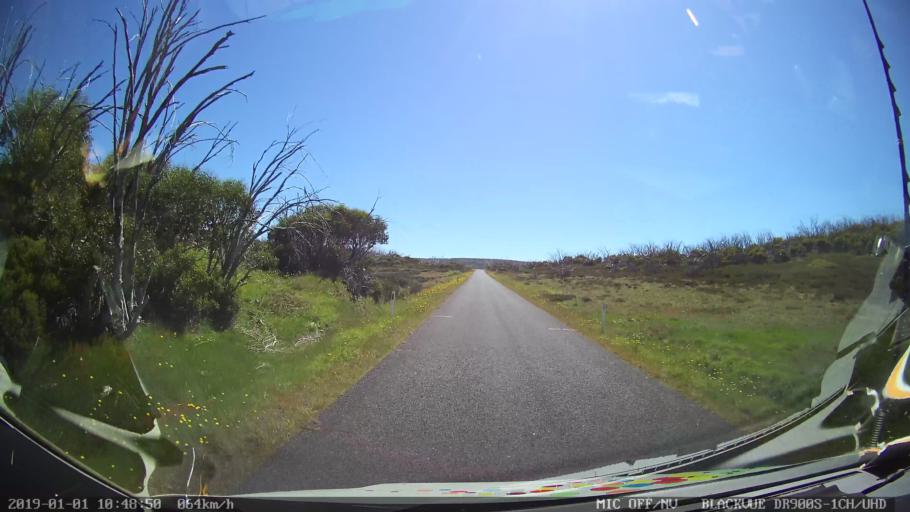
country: AU
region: New South Wales
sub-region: Snowy River
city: Jindabyne
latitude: -36.0377
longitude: 148.3645
